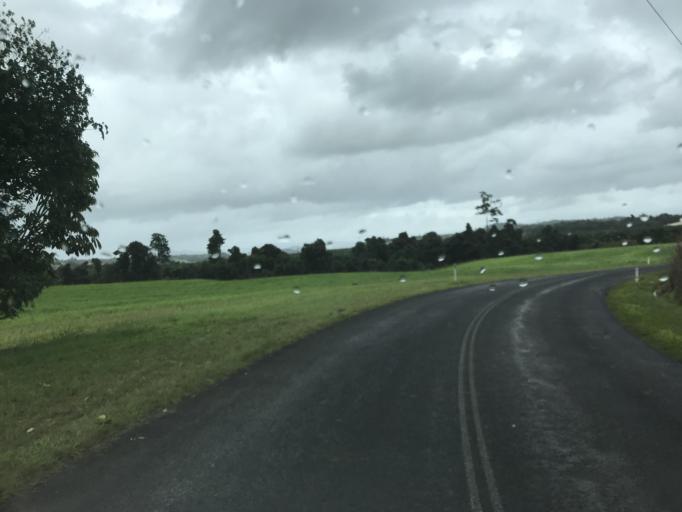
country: AU
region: Queensland
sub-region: Cassowary Coast
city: Innisfail
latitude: -17.5193
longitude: 145.9711
